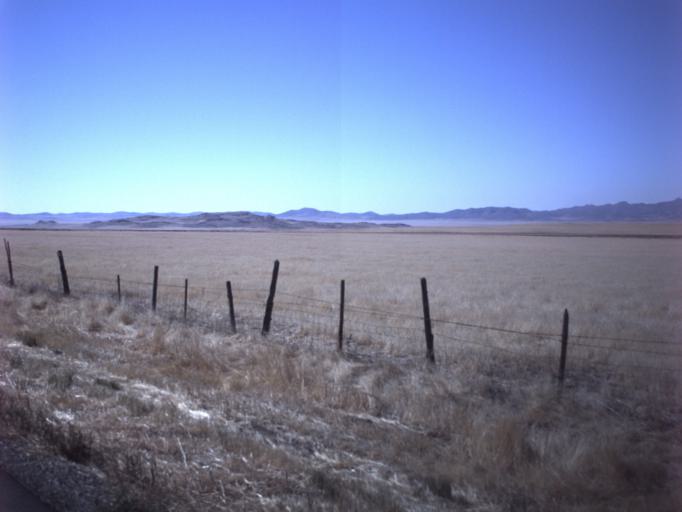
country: US
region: Utah
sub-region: Tooele County
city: Grantsville
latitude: 40.4298
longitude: -112.7487
